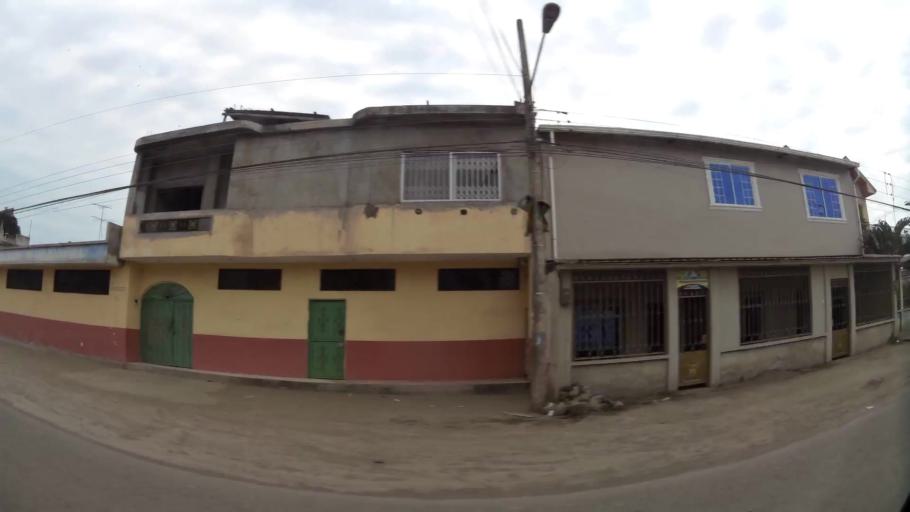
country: EC
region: El Oro
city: Machala
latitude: -3.2688
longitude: -79.9339
